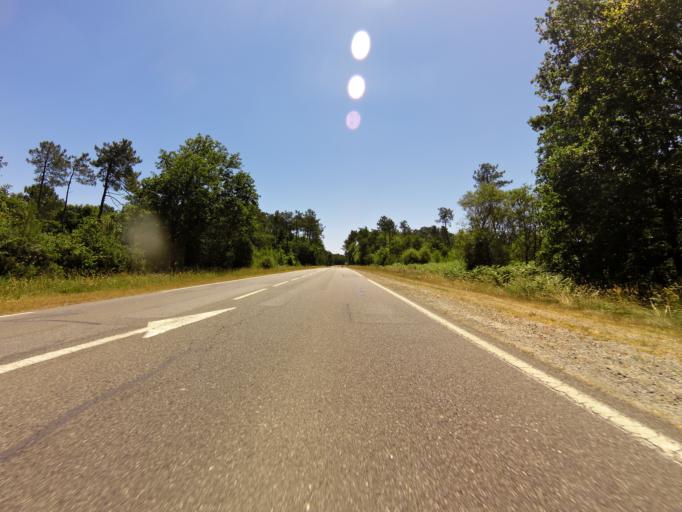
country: FR
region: Brittany
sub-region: Departement du Morbihan
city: Ferel
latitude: 47.4876
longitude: -2.3873
